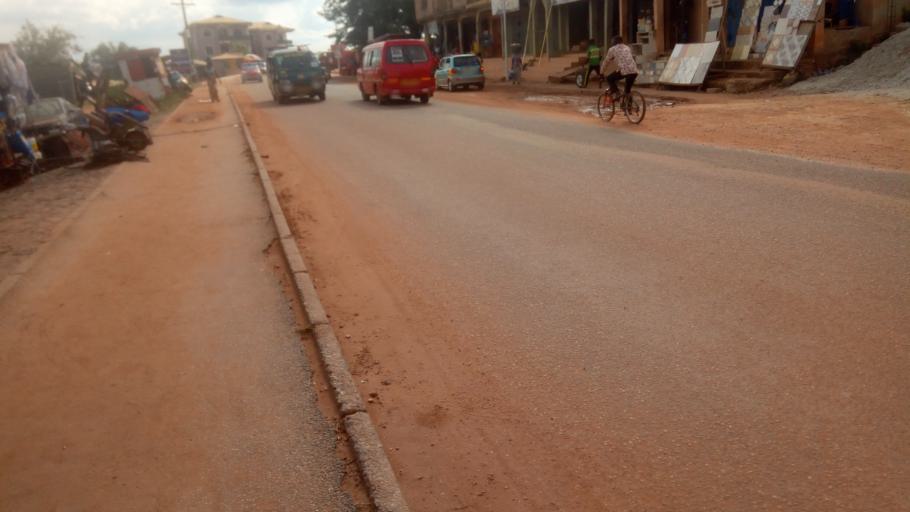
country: GH
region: Ashanti
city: Obuasi
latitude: 6.2112
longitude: -1.6877
